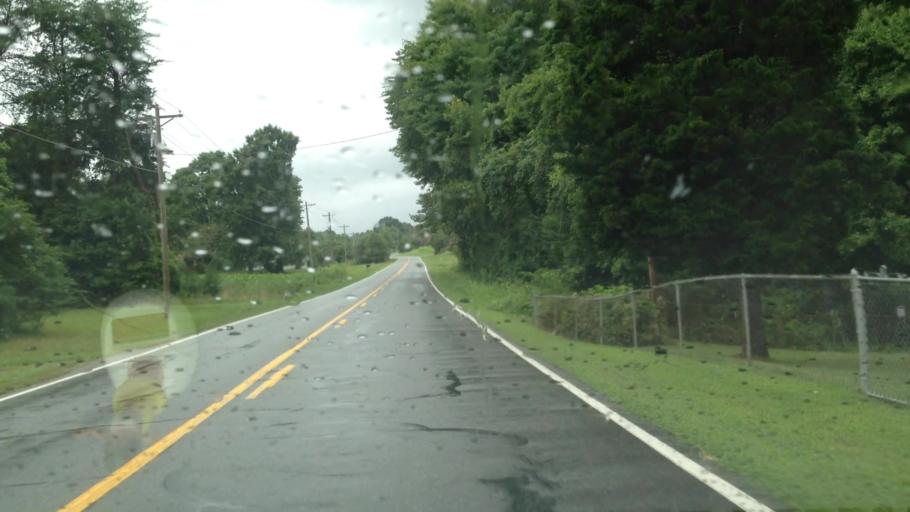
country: US
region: North Carolina
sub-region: Stokes County
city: Walnut Cove
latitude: 36.2649
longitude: -80.0948
